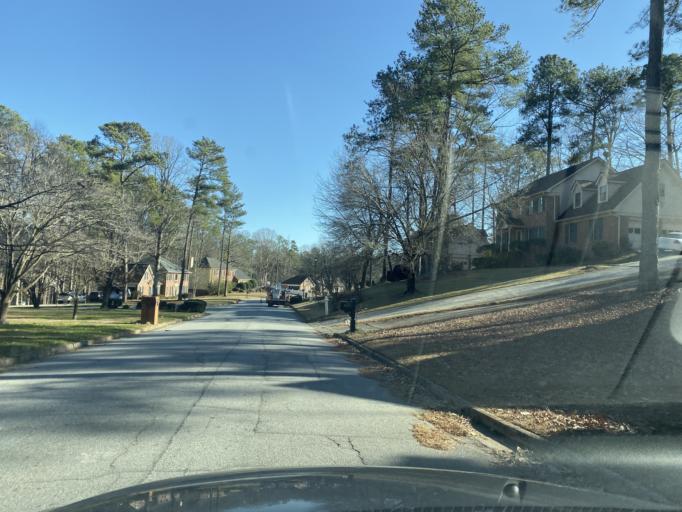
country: US
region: Georgia
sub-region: DeKalb County
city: Pine Mountain
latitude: 33.6807
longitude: -84.1583
